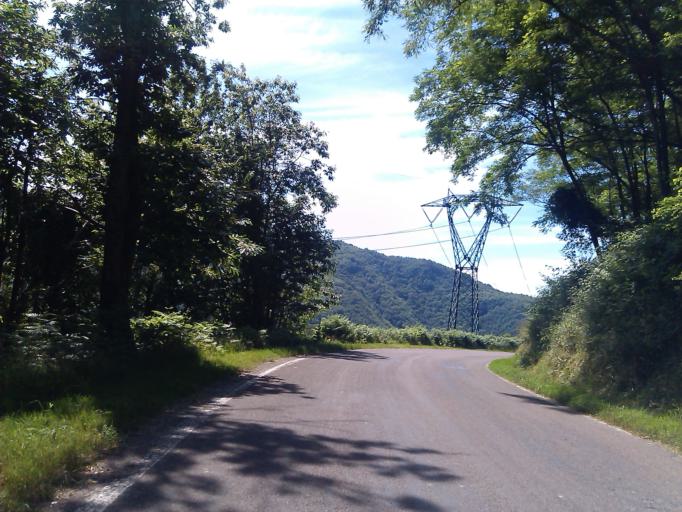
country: IT
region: Tuscany
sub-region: Provincia di Pistoia
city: Sambuca Pistoiese
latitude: 44.0986
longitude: 11.0447
